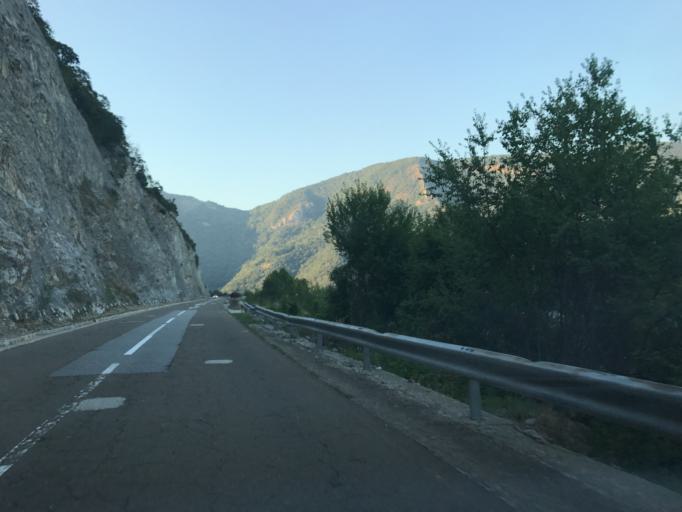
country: RO
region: Caras-Severin
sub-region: Comuna Berzasca
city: Berzasca
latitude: 44.5841
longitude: 22.0205
